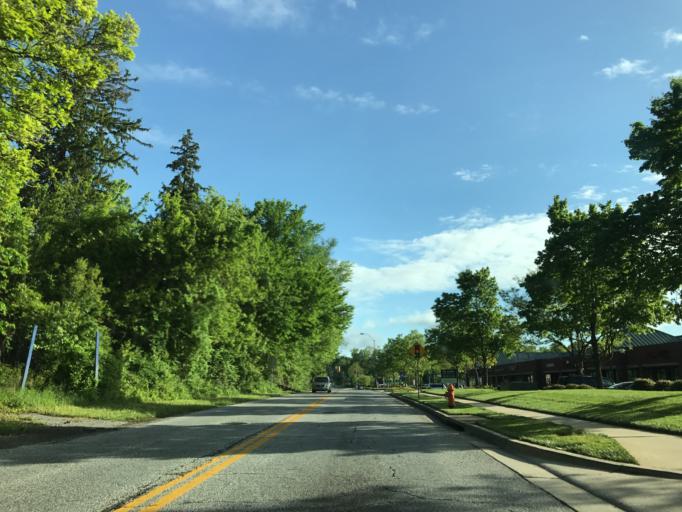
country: US
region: Maryland
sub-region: Baltimore County
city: Owings Mills
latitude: 39.4222
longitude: -76.8069
